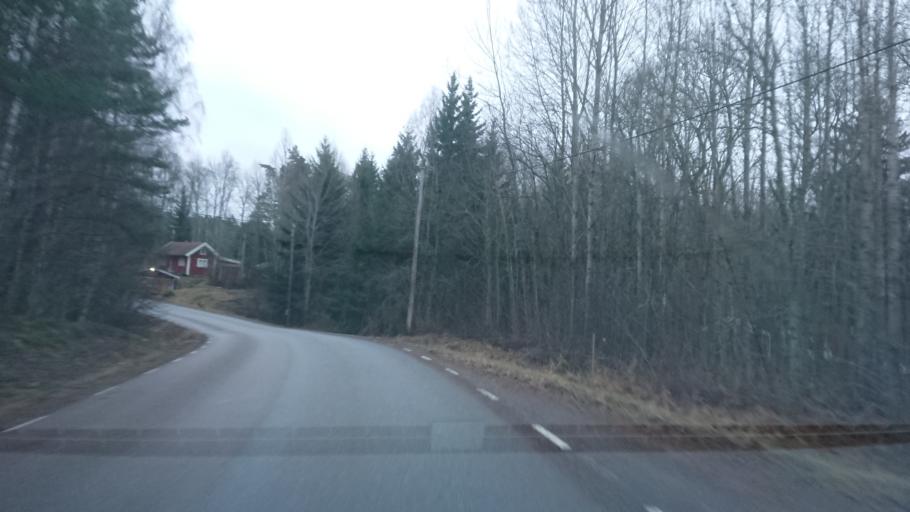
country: SE
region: Uppsala
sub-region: Osthammars Kommun
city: Bjorklinge
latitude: 60.0208
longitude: 17.5750
